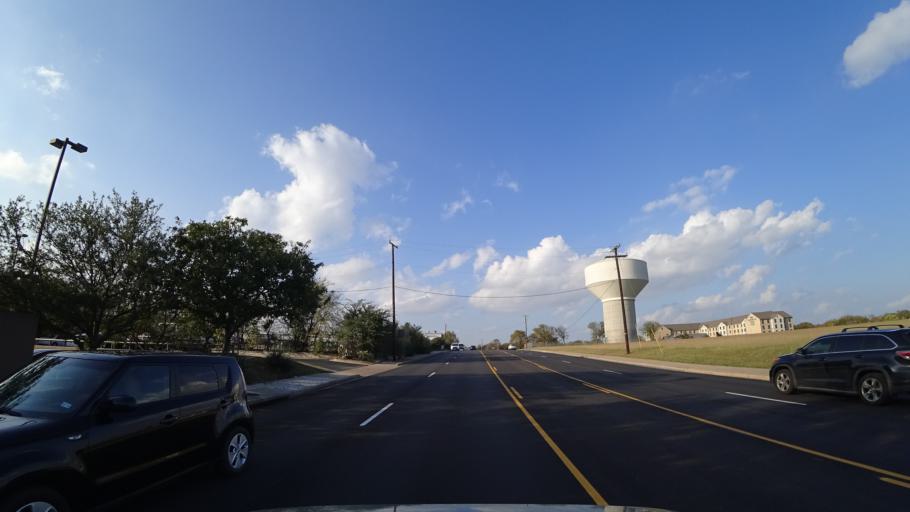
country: US
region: Texas
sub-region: Williamson County
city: Round Rock
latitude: 30.4876
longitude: -97.6737
